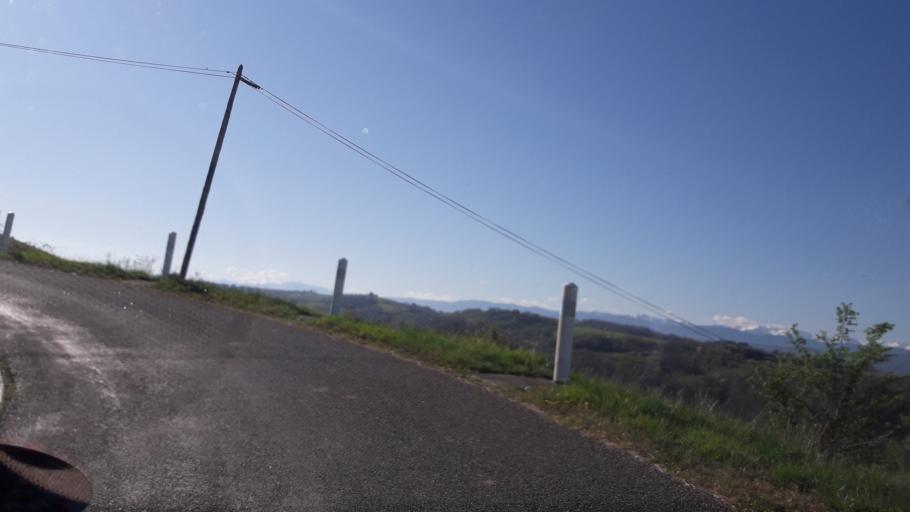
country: FR
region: Midi-Pyrenees
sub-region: Departement de la Haute-Garonne
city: Montesquieu-Volvestre
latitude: 43.2020
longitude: 1.2751
